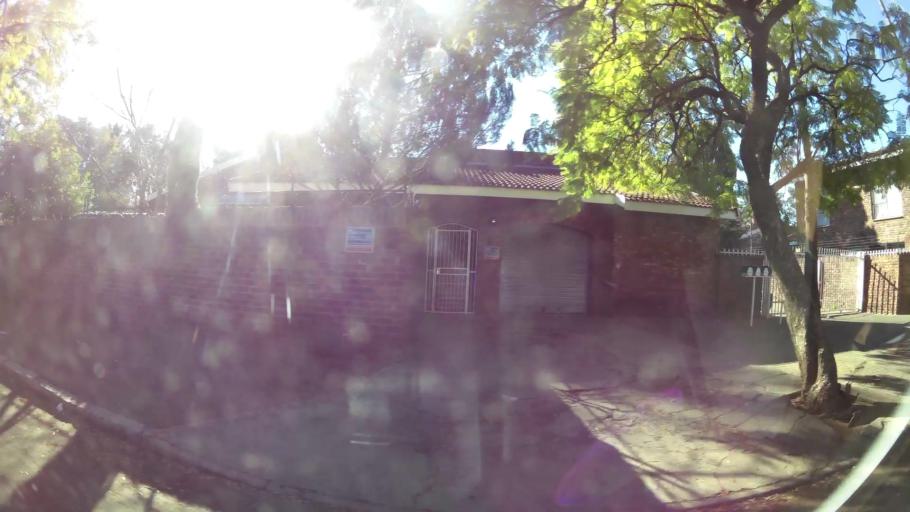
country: ZA
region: Northern Cape
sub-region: Frances Baard District Municipality
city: Kimberley
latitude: -28.7462
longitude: 24.7767
